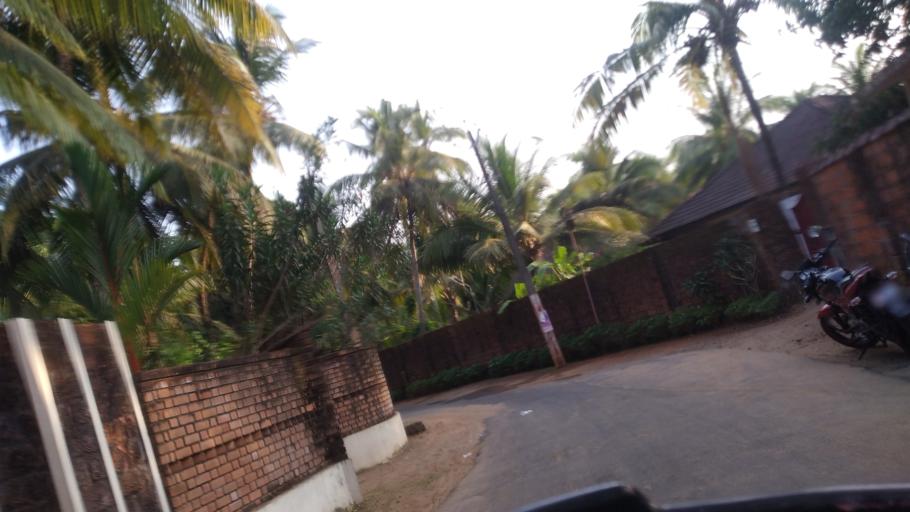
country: IN
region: Kerala
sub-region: Thrissur District
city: Thanniyam
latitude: 10.4227
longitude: 76.0826
